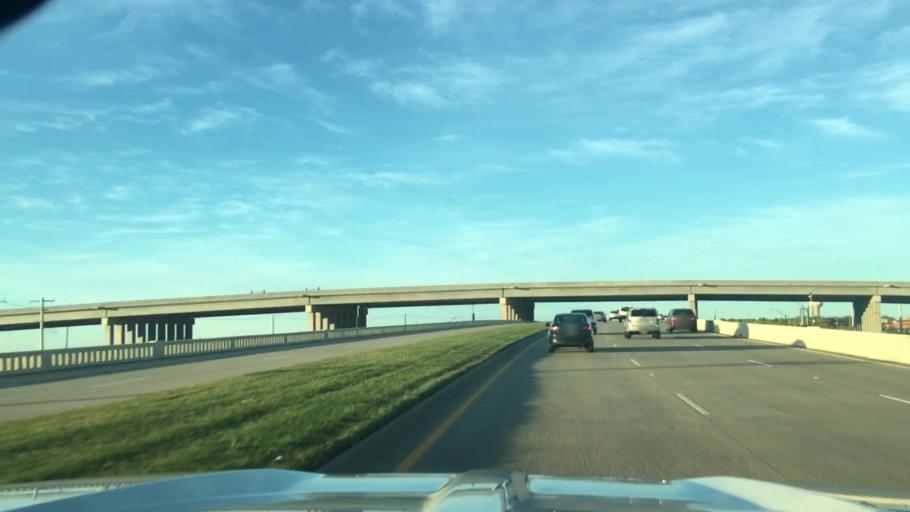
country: US
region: Texas
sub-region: Collin County
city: Prosper
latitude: 33.2171
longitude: -96.8024
